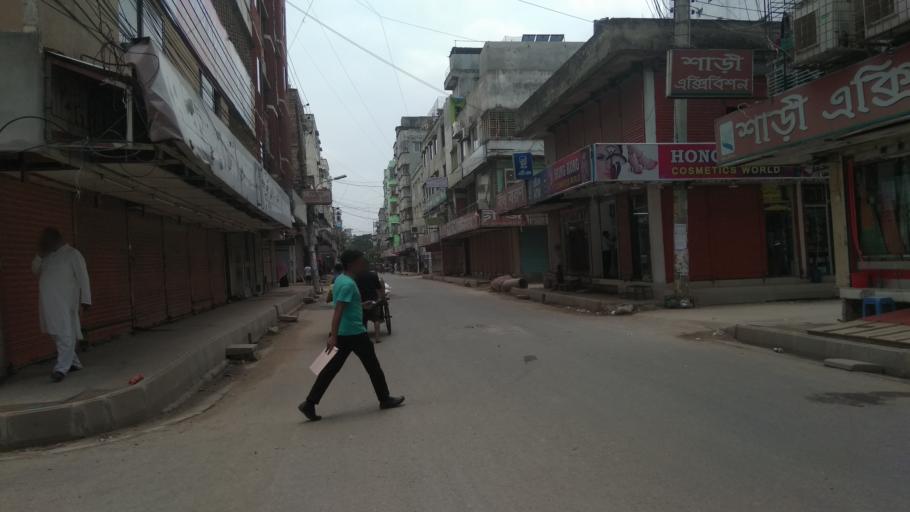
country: BD
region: Dhaka
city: Azimpur
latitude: 23.8114
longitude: 90.3699
